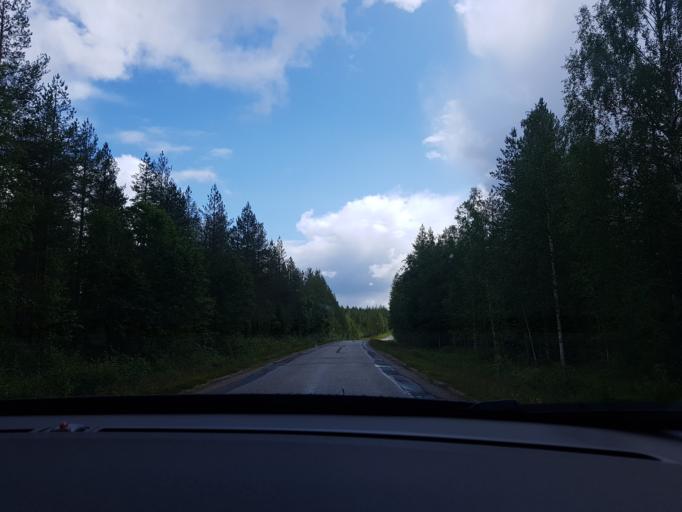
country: FI
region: Kainuu
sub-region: Kehys-Kainuu
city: Kuhmo
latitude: 64.4604
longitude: 29.6292
